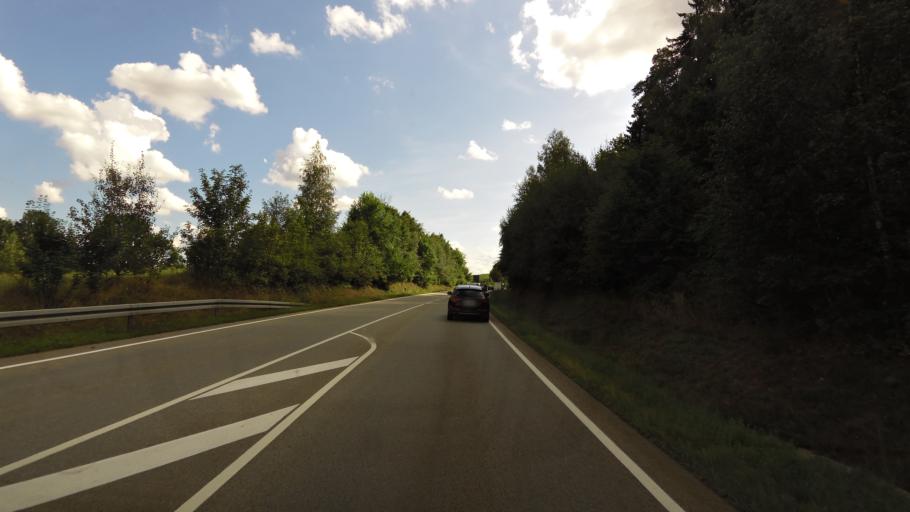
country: DE
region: Bavaria
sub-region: Lower Bavaria
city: Rattiszell
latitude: 49.0311
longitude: 12.6545
